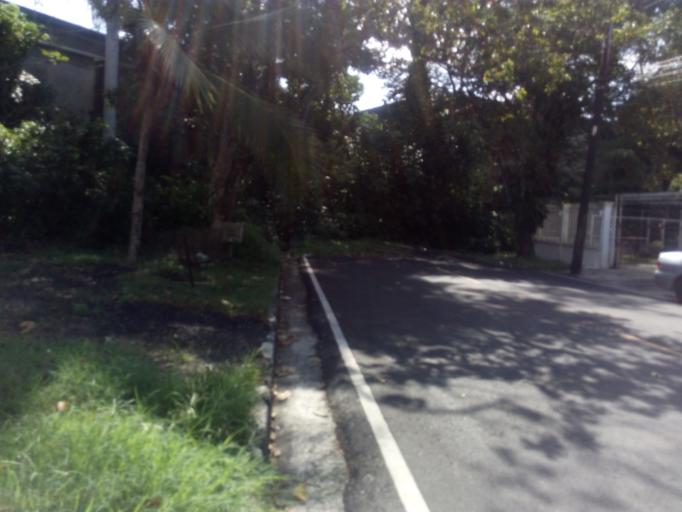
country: PA
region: Panama
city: Panama
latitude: 8.9918
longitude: -79.5378
